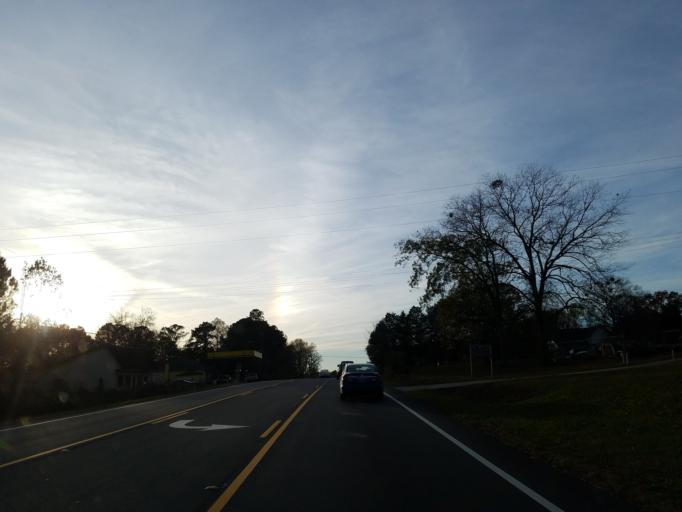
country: US
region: Georgia
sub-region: Haralson County
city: Bremen
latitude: 33.7216
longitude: -85.1133
